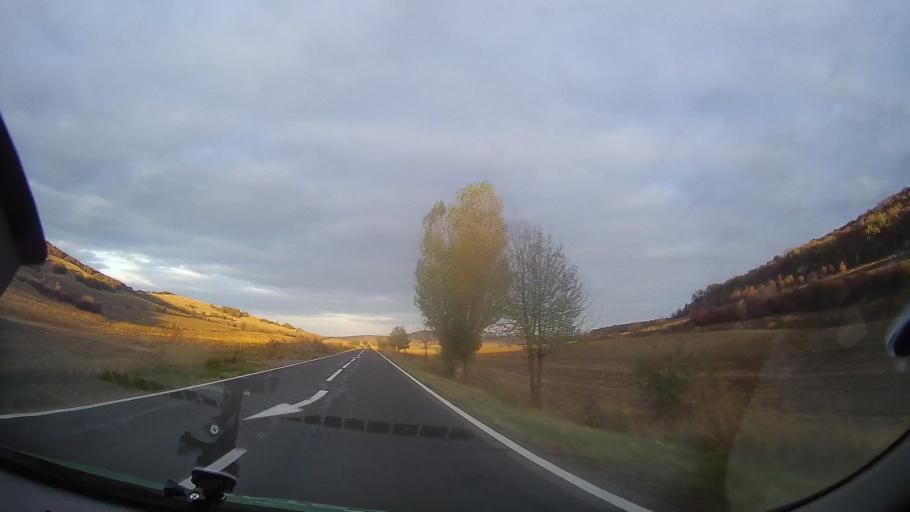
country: RO
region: Tulcea
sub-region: Comuna Ciucurova
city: Ciucurova
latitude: 44.9622
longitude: 28.5219
